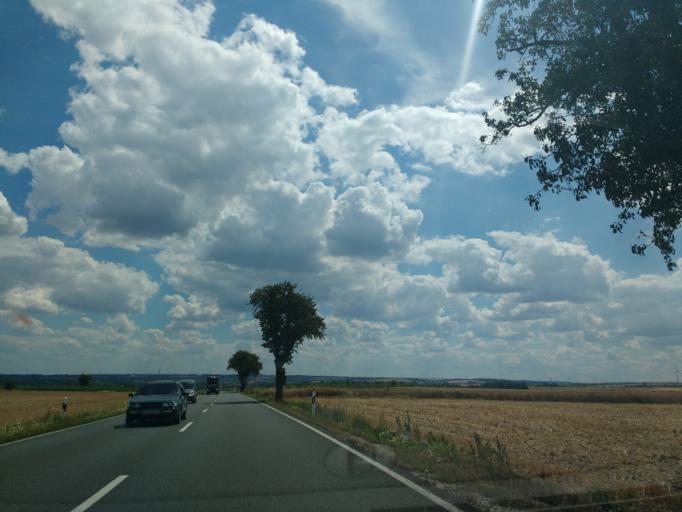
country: DE
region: Saxony-Anhalt
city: Droyssig
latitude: 51.0703
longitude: 12.0428
